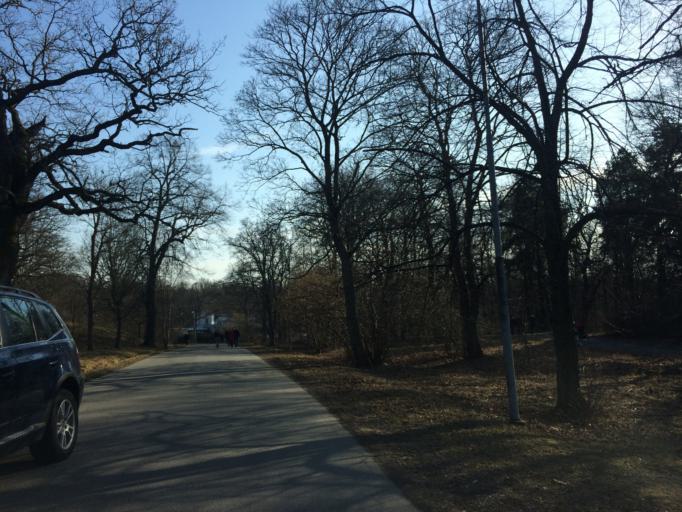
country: SE
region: Stockholm
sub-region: Stockholms Kommun
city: OEstermalm
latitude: 59.3251
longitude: 18.1162
